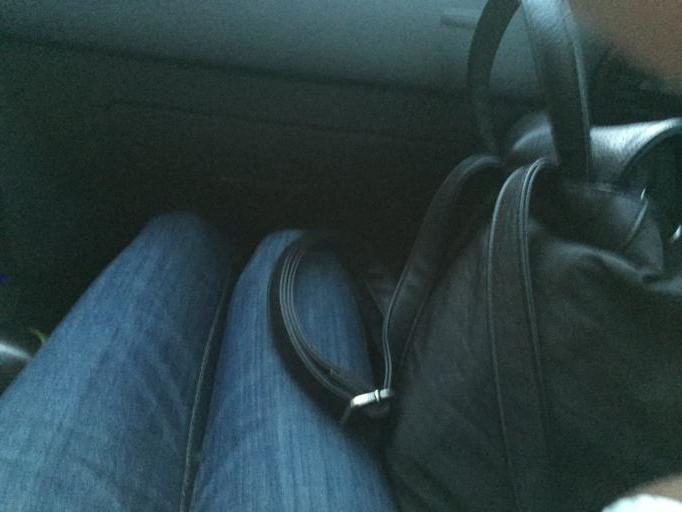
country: MX
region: Veracruz
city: Maltrata
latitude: 18.8267
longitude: -97.2852
